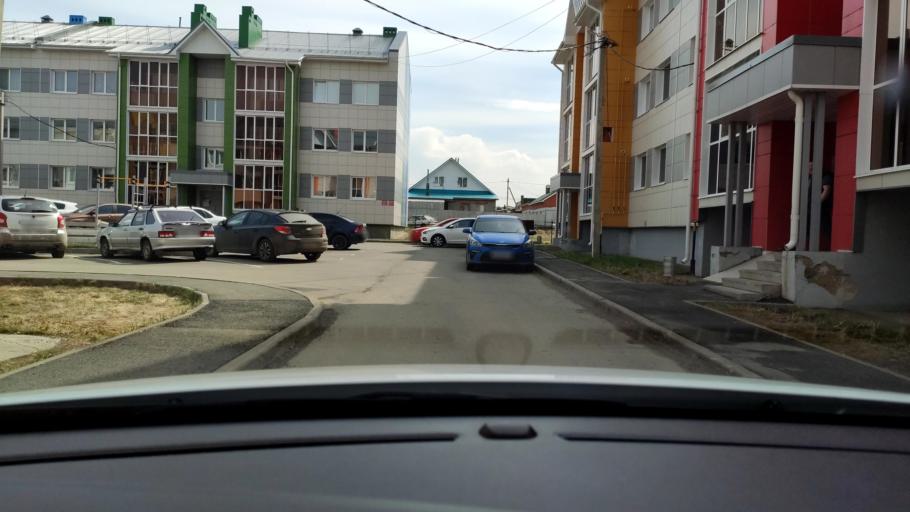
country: RU
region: Tatarstan
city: Vysokaya Gora
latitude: 55.9138
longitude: 49.3123
